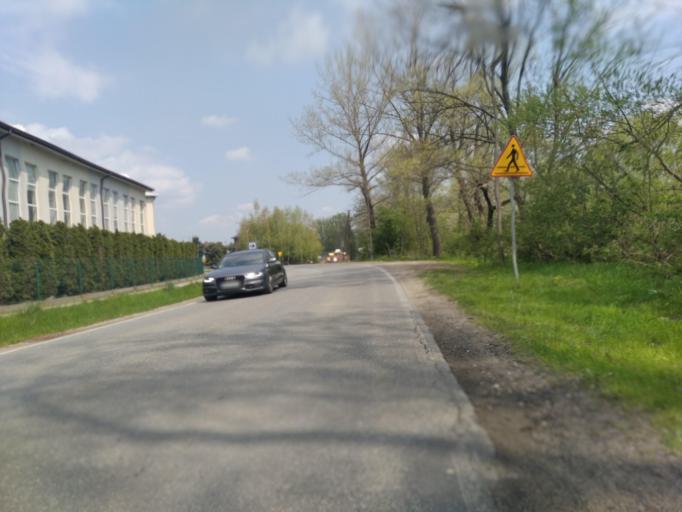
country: PL
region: Subcarpathian Voivodeship
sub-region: Powiat krosnienski
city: Rymanow
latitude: 49.5622
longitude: 21.8587
